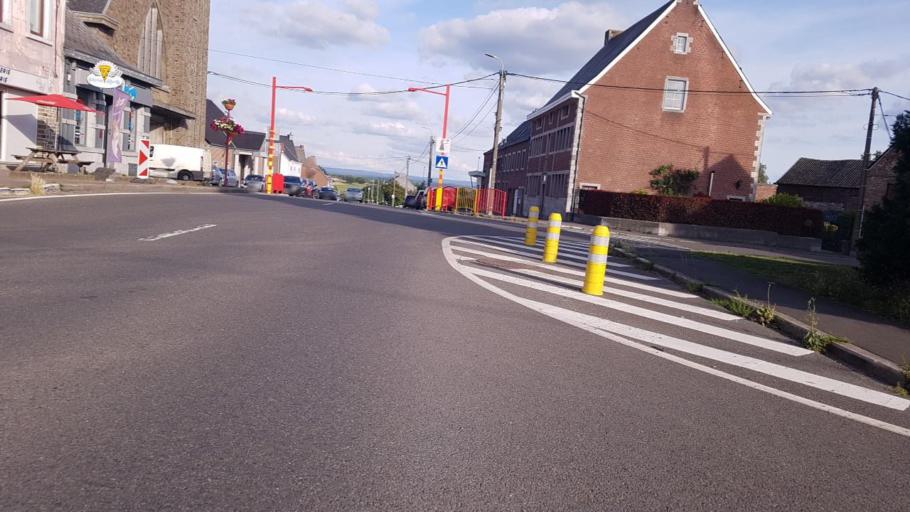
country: BE
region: Wallonia
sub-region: Province de Liege
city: Soumagne
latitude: 50.6090
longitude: 5.7136
